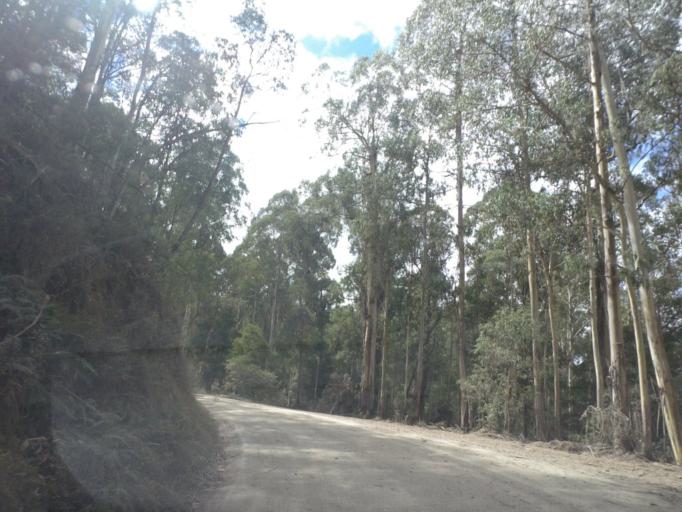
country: AU
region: Victoria
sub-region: Yarra Ranges
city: Millgrove
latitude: -37.5230
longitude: 145.9457
